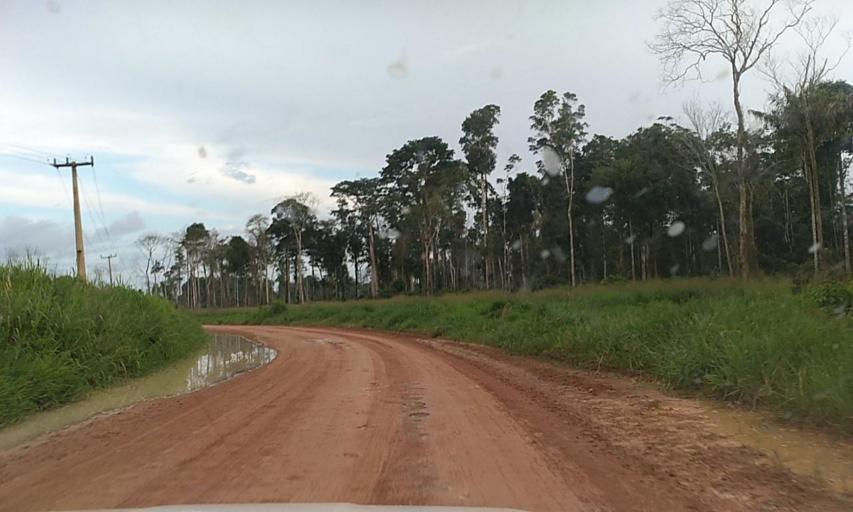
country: BR
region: Para
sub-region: Senador Jose Porfirio
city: Senador Jose Porfirio
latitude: -2.7060
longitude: -51.8118
